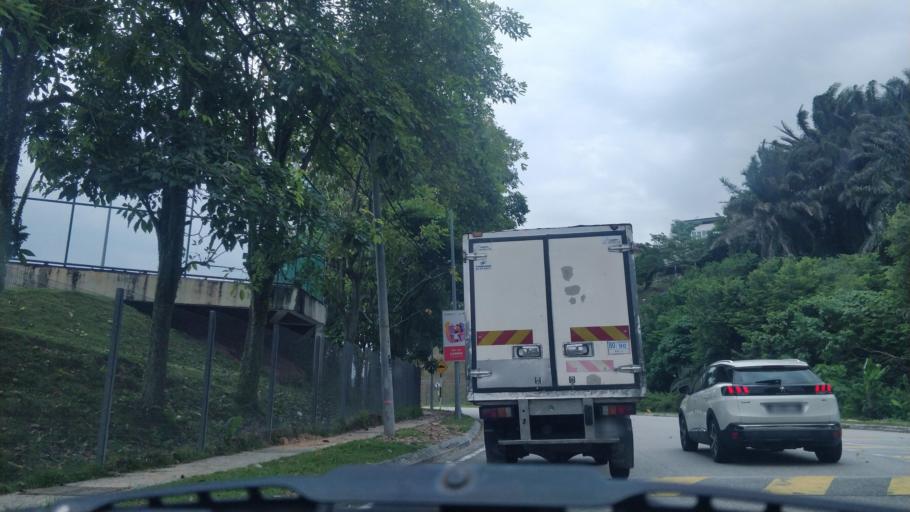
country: MY
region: Selangor
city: Kuang
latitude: 3.2045
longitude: 101.5877
